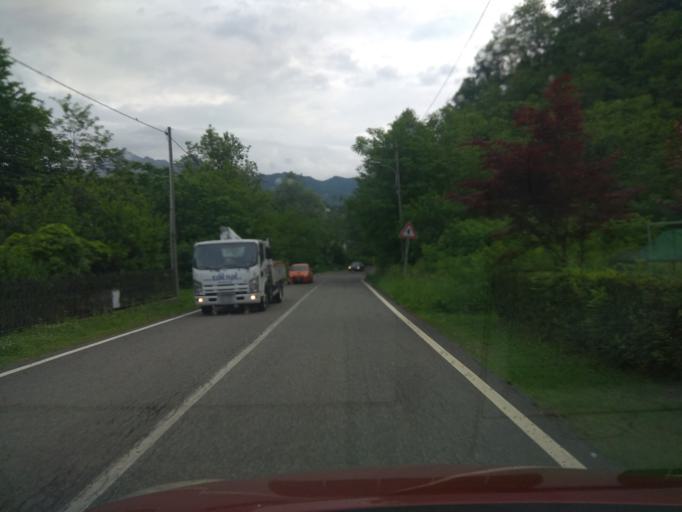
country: IT
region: Piedmont
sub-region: Provincia di Biella
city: Pray
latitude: 45.6691
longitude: 8.2127
